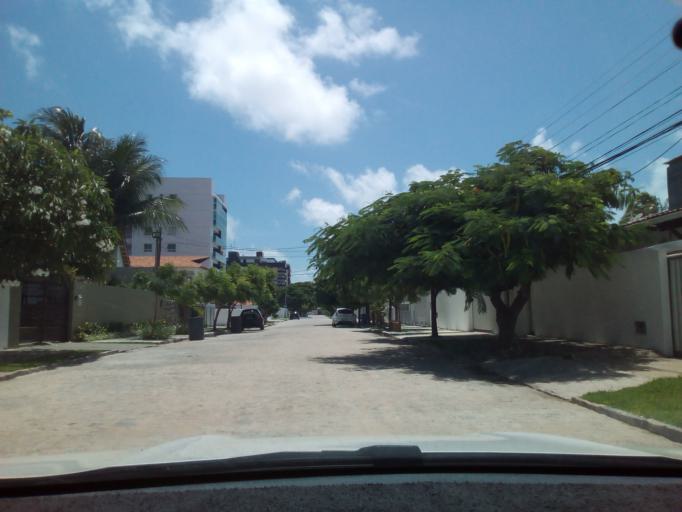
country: BR
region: Paraiba
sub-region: Cabedelo
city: Cabedelo
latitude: -6.9983
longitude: -34.8272
